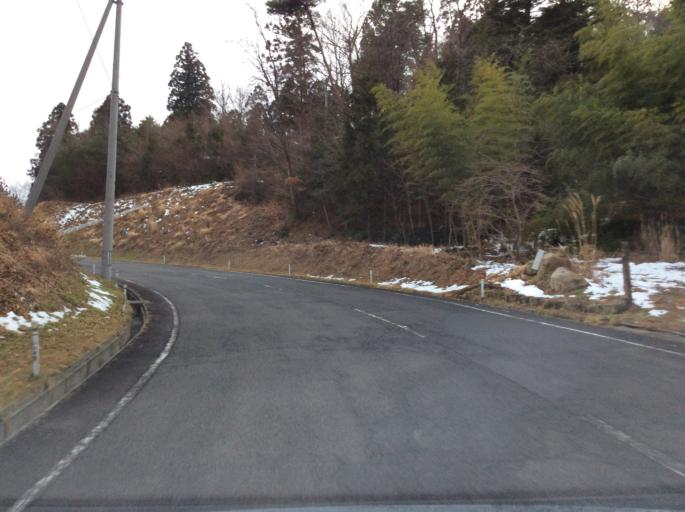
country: JP
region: Fukushima
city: Iwaki
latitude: 37.1715
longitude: 140.9404
